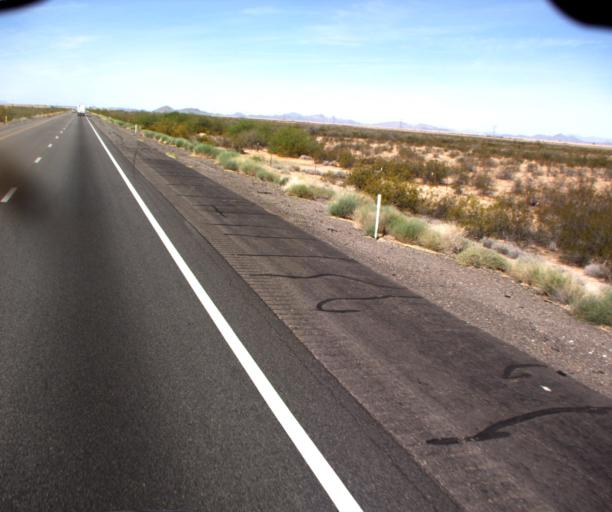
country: US
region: Arizona
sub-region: La Paz County
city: Salome
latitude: 33.5664
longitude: -113.3338
